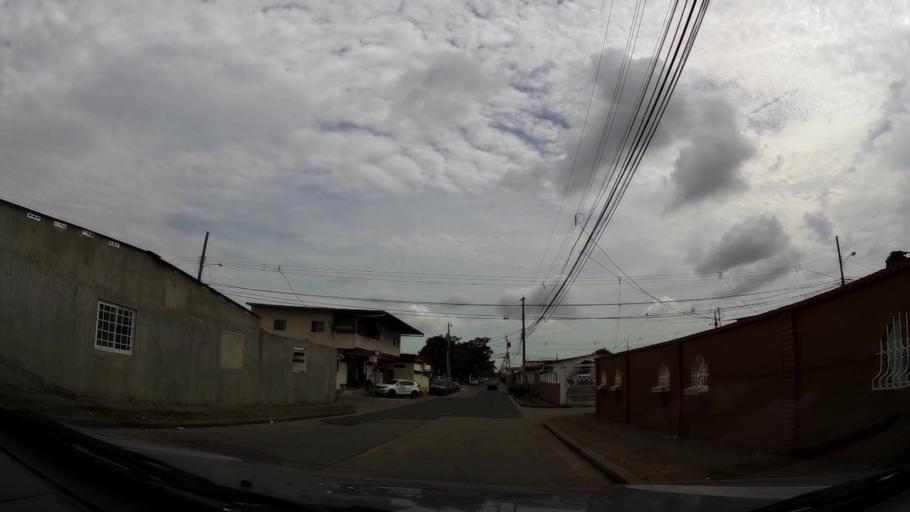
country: PA
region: Panama
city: Tocumen
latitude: 9.0507
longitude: -79.4168
